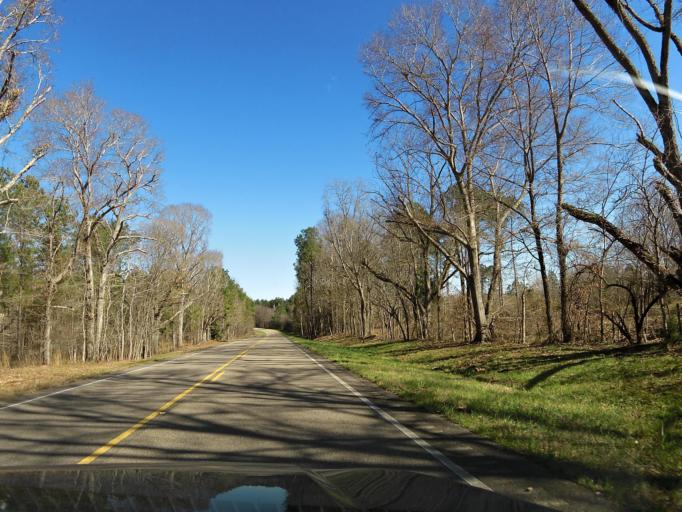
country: US
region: Alabama
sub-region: Bullock County
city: Union Springs
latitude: 32.1108
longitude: -85.7915
